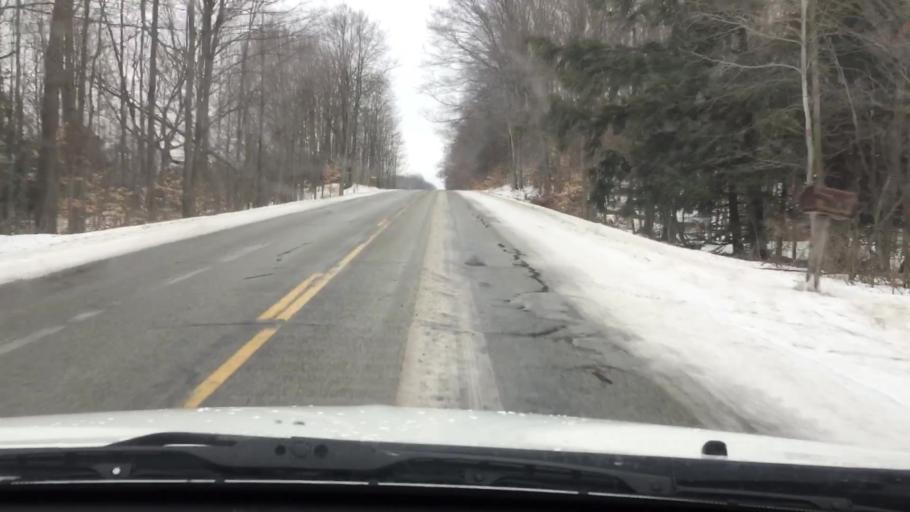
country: US
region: Michigan
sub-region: Wexford County
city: Cadillac
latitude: 44.1835
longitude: -85.4055
